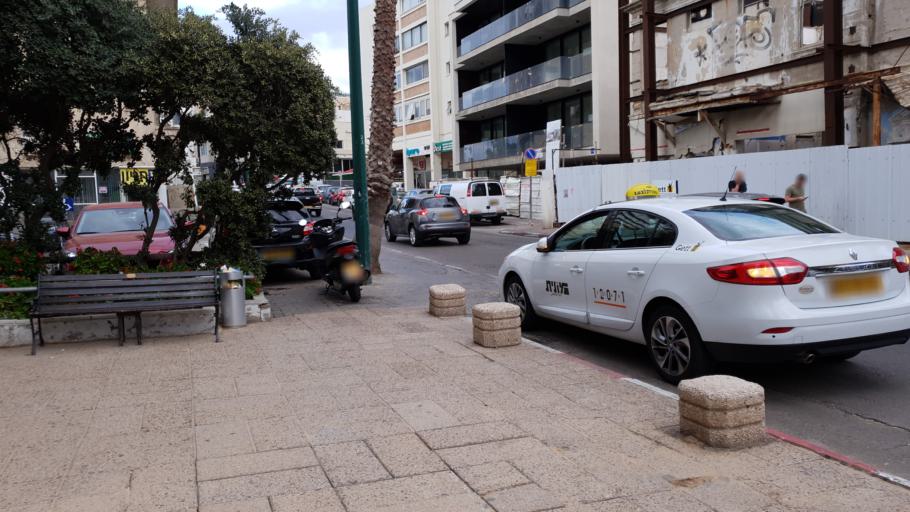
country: IL
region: Tel Aviv
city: Tel Aviv
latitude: 32.0800
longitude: 34.7681
